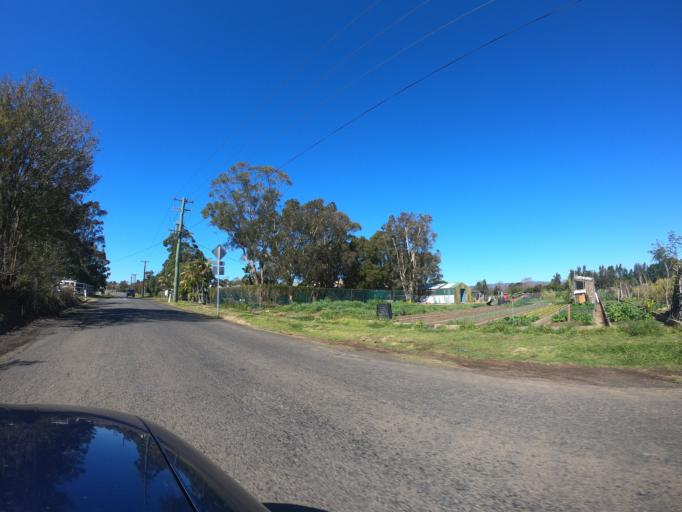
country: AU
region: New South Wales
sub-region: Wollongong
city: Koonawarra
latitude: -34.4811
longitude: 150.7993
